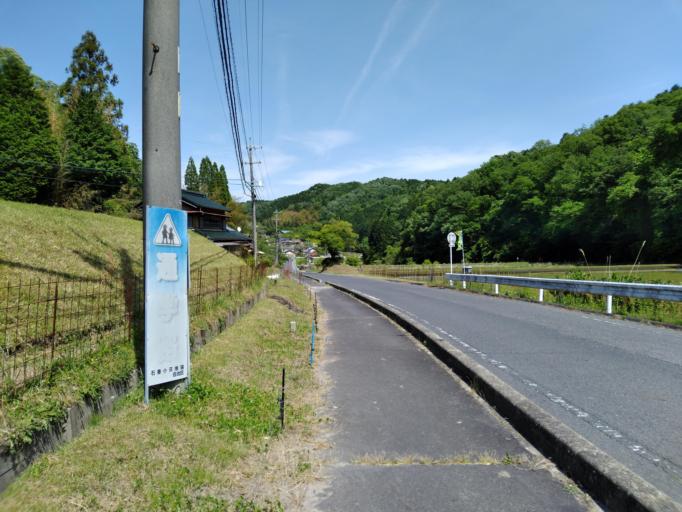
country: JP
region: Gifu
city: Tajimi
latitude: 35.2428
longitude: 137.2175
